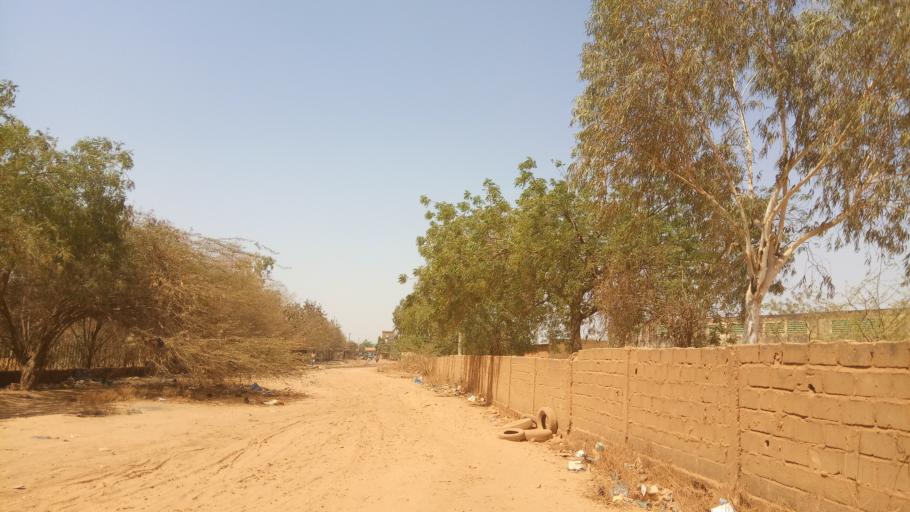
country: BF
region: Centre
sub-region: Kadiogo Province
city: Ouagadougou
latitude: 12.3939
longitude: -1.5698
